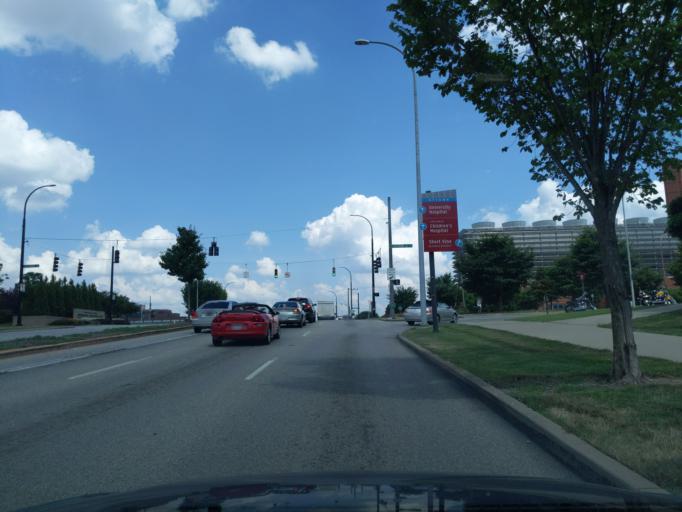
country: US
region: Ohio
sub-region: Hamilton County
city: Saint Bernard
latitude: 39.1354
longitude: -84.5112
